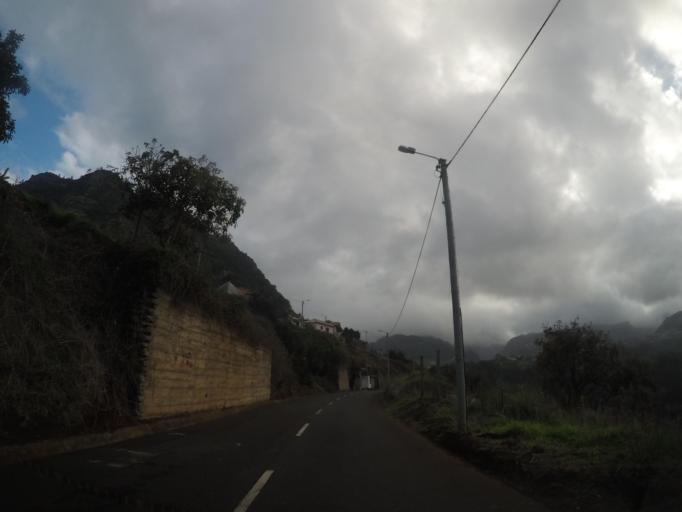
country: PT
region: Madeira
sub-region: Santana
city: Santana
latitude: 32.7890
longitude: -16.8483
